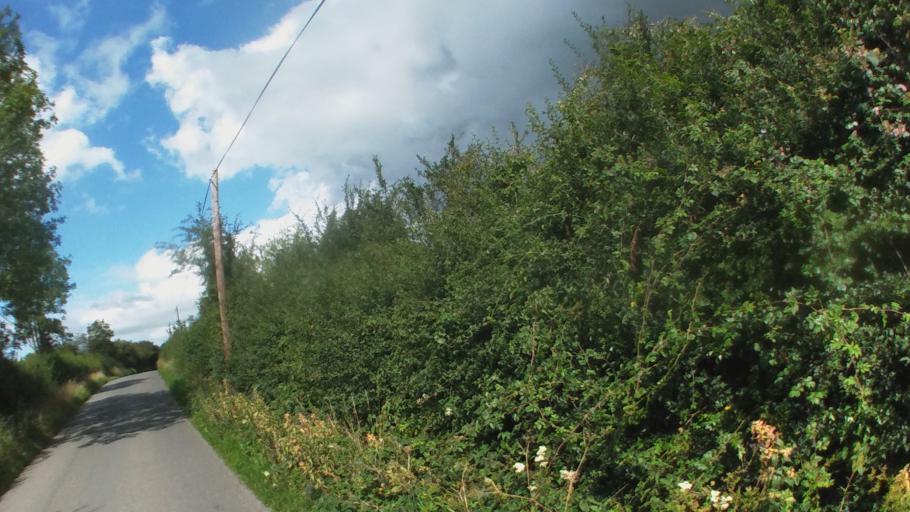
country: IE
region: Leinster
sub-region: Kilkenny
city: Kilkenny
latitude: 52.6814
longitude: -7.2211
